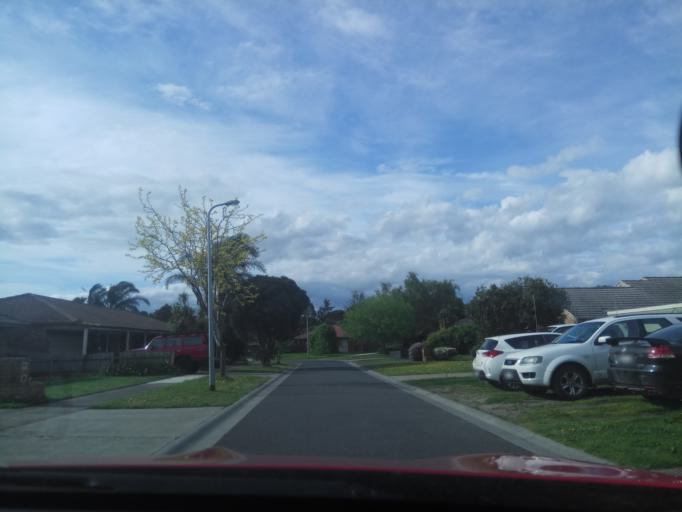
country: AU
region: Victoria
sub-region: Casey
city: Cranbourne North
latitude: -38.0719
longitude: 145.2731
